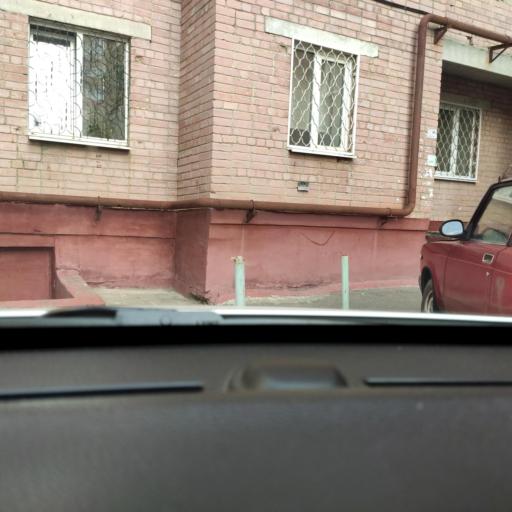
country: RU
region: Voronezj
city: Podgornoye
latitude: 51.7108
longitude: 39.1493
